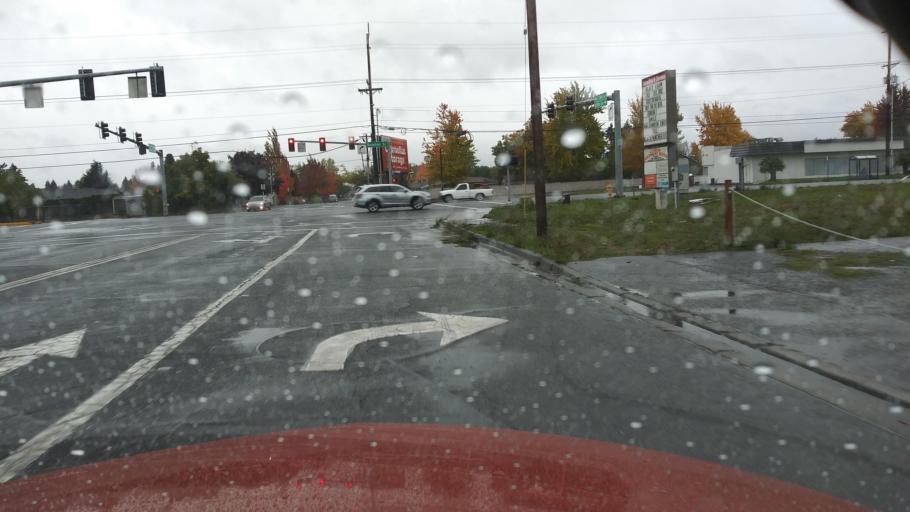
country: US
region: Oregon
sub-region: Washington County
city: Cornelius
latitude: 45.5205
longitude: -123.0398
